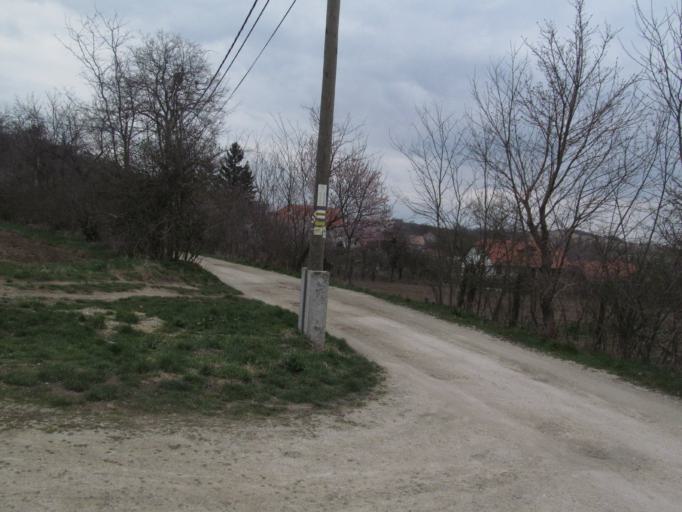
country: HU
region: Gyor-Moson-Sopron
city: Pannonhalma
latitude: 47.5488
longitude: 17.7694
